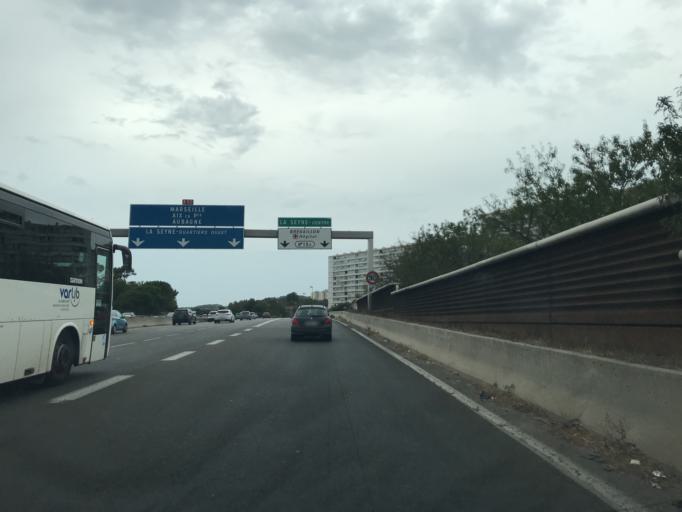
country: FR
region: Provence-Alpes-Cote d'Azur
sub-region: Departement du Var
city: La Seyne-sur-Mer
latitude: 43.1255
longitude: 5.8990
